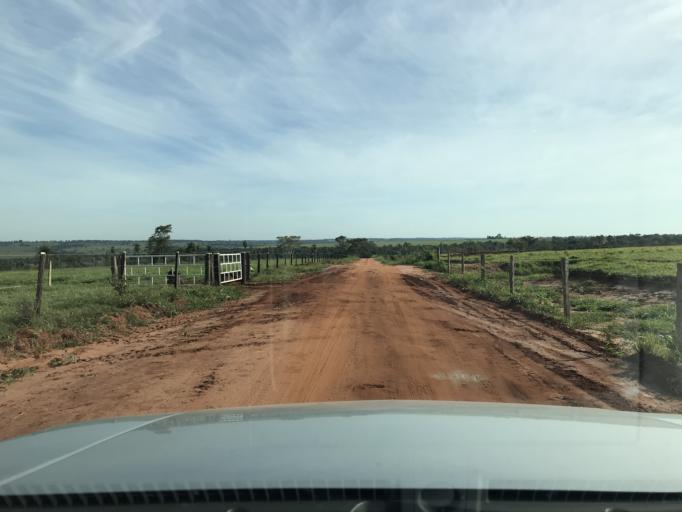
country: BR
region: Mato Grosso do Sul
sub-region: Iguatemi
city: Iguatemi
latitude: -23.6527
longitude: -54.5739
